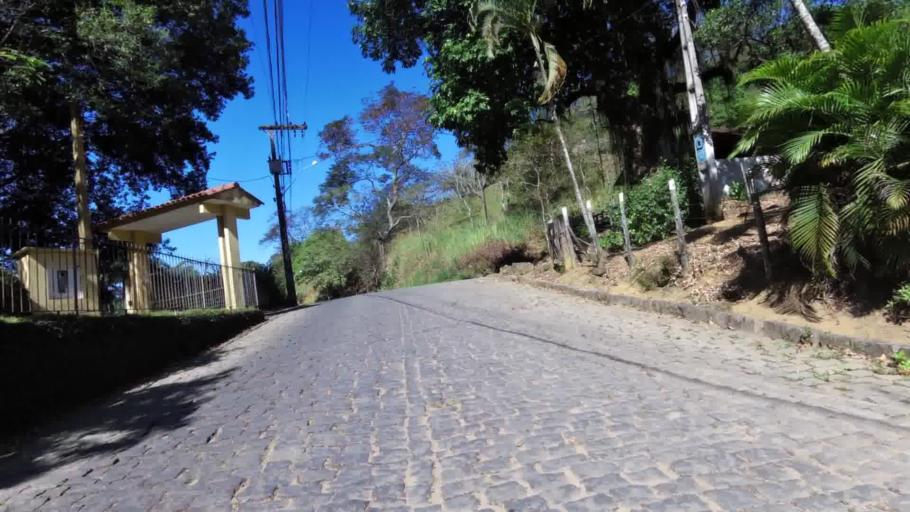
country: BR
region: Espirito Santo
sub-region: Rio Novo Do Sul
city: Rio Novo do Sul
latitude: -20.8566
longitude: -40.9312
